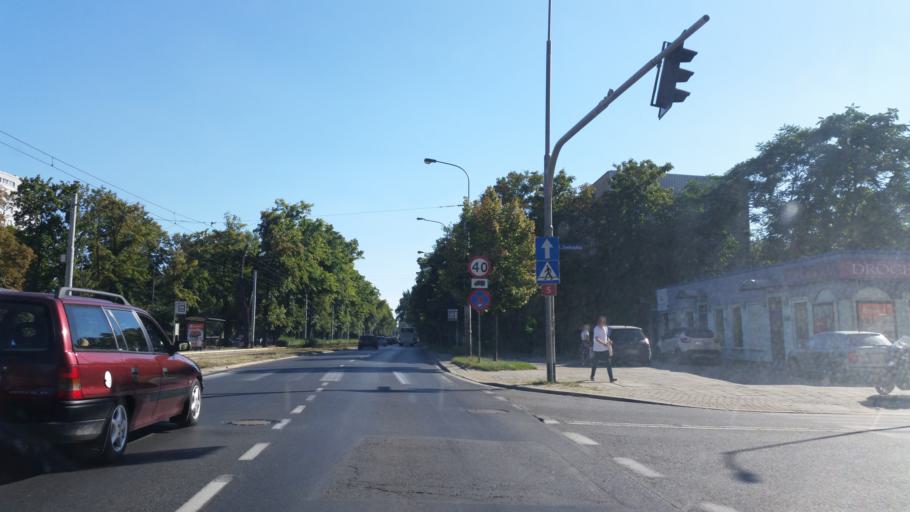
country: PL
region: Lower Silesian Voivodeship
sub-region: Powiat wroclawski
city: Wroclaw
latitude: 51.0842
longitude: 17.0104
